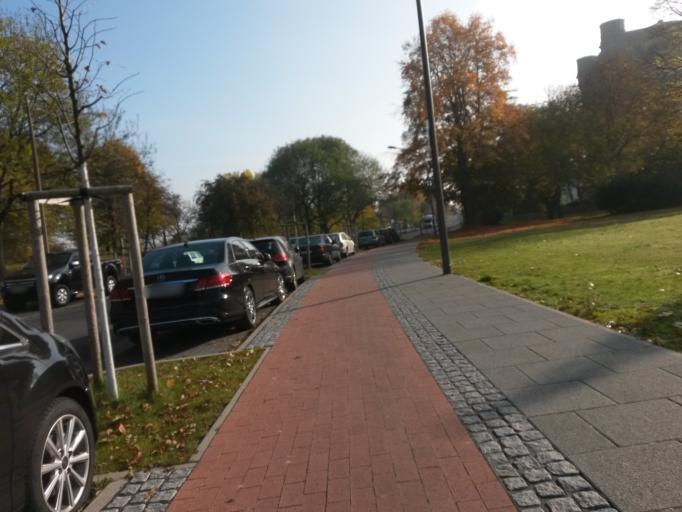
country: DE
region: Bremen
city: Bremen
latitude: 53.0697
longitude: 8.8090
